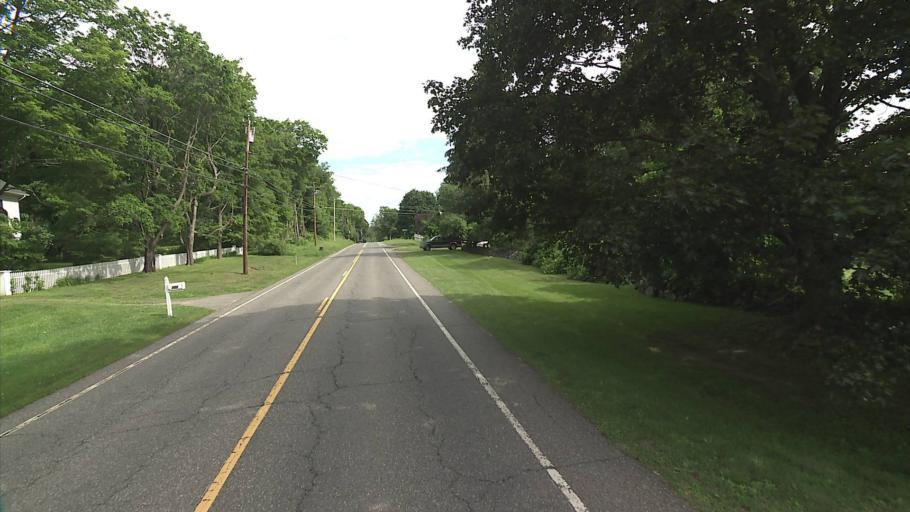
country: US
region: Connecticut
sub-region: Litchfield County
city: Litchfield
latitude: 41.6952
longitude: -73.1829
